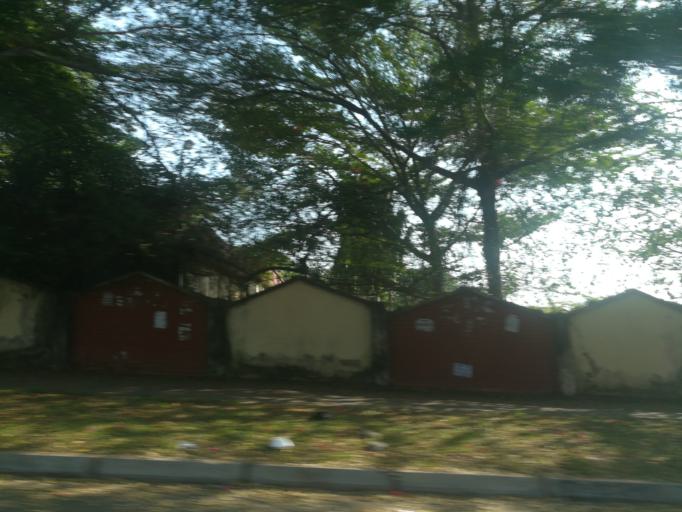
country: NG
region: Abuja Federal Capital Territory
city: Abuja
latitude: 9.0717
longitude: 7.4406
